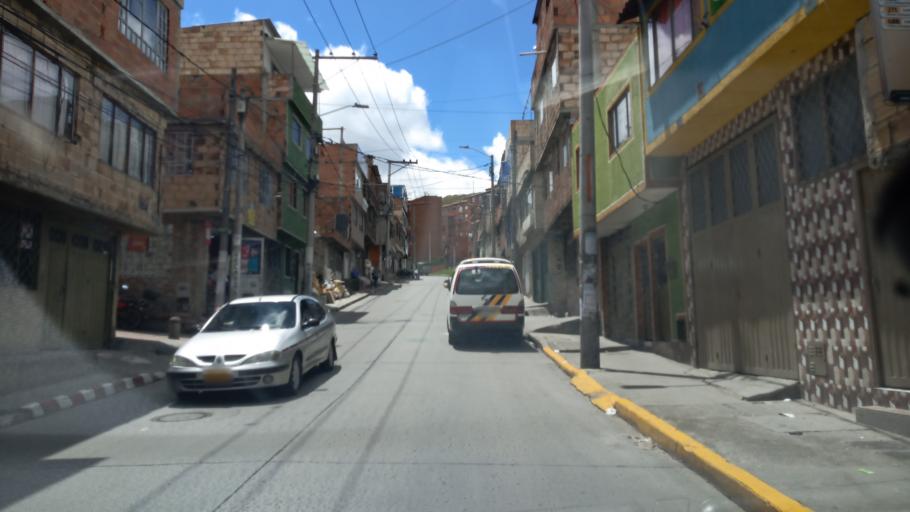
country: CO
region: Bogota D.C.
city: Bogota
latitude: 4.5654
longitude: -74.1117
